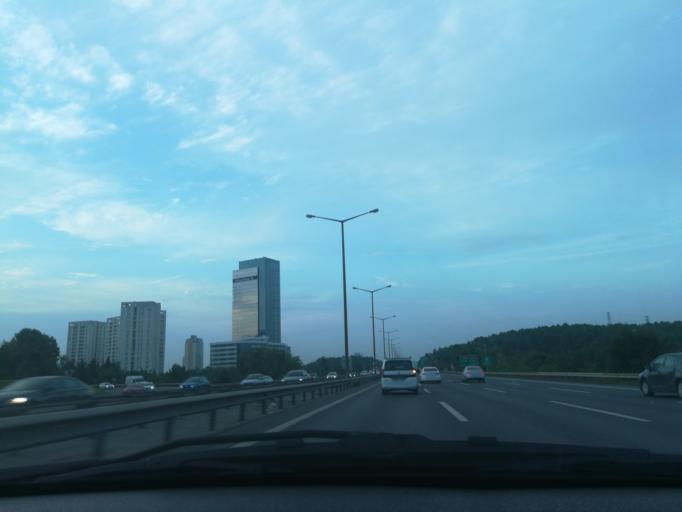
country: TR
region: Istanbul
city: Umraniye
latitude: 41.0310
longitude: 29.1211
